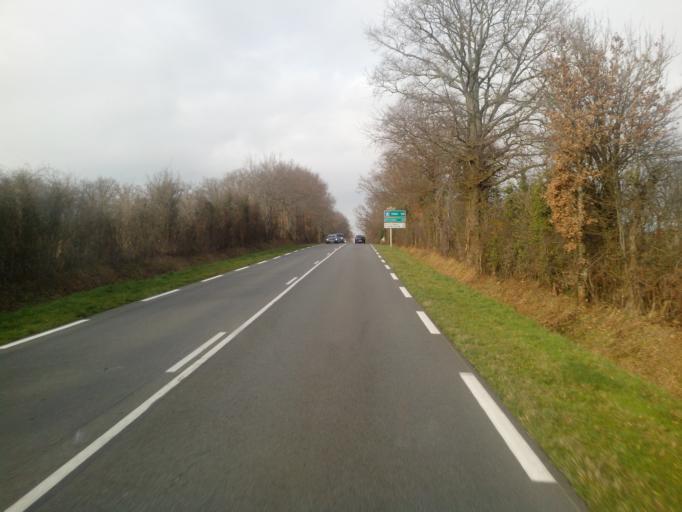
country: FR
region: Limousin
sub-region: Departement de la Haute-Vienne
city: Bussiere-Poitevine
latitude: 46.2761
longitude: 0.8583
